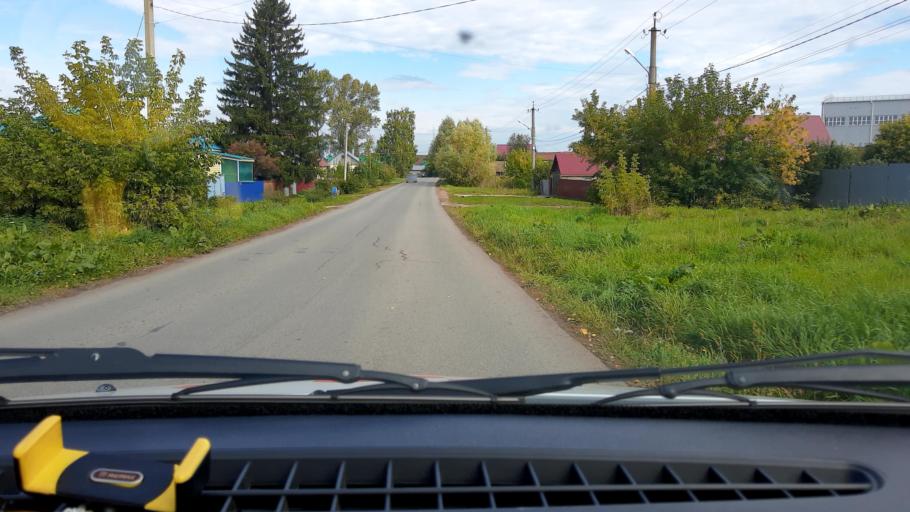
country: RU
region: Bashkortostan
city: Blagoveshchensk
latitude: 55.0353
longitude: 55.9831
